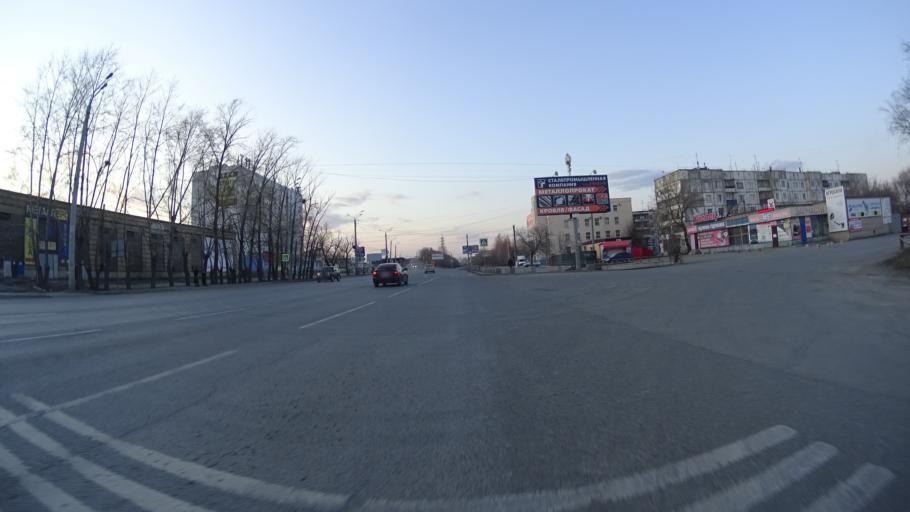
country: RU
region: Chelyabinsk
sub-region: Gorod Chelyabinsk
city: Chelyabinsk
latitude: 55.1119
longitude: 61.3869
